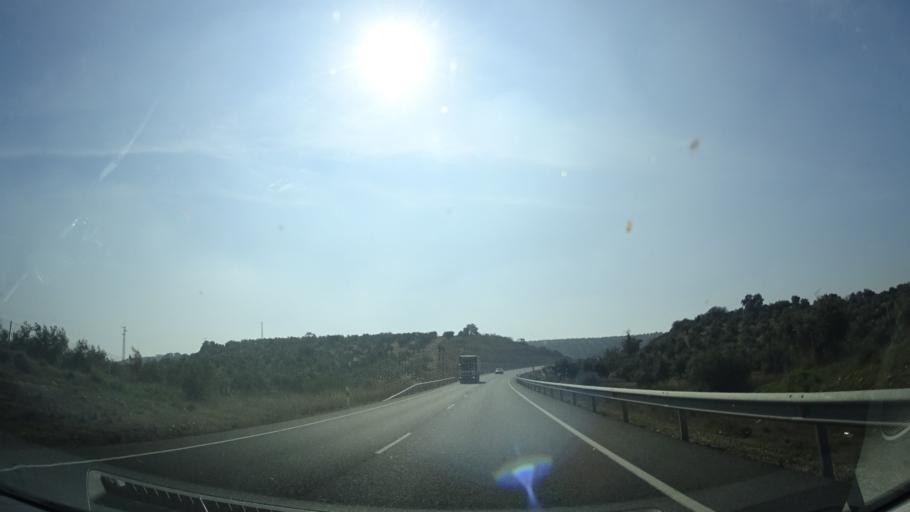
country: ES
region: Andalusia
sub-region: Province of Cordoba
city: Montoro
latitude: 38.0222
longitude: -4.3690
